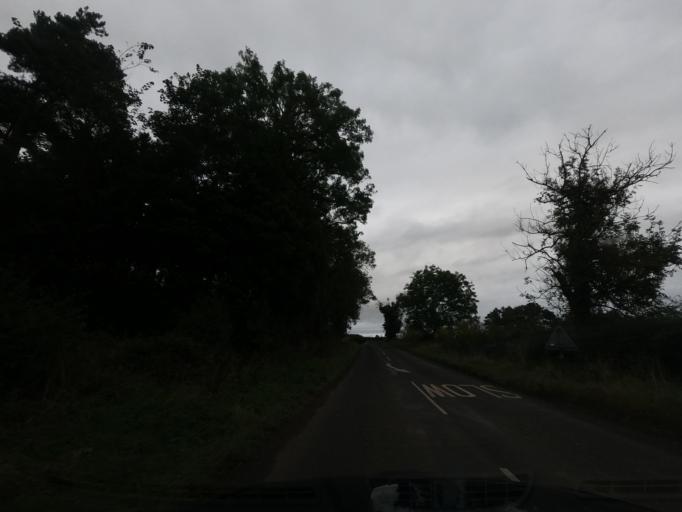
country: GB
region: England
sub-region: Northumberland
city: Ford
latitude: 55.6785
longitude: -2.0946
